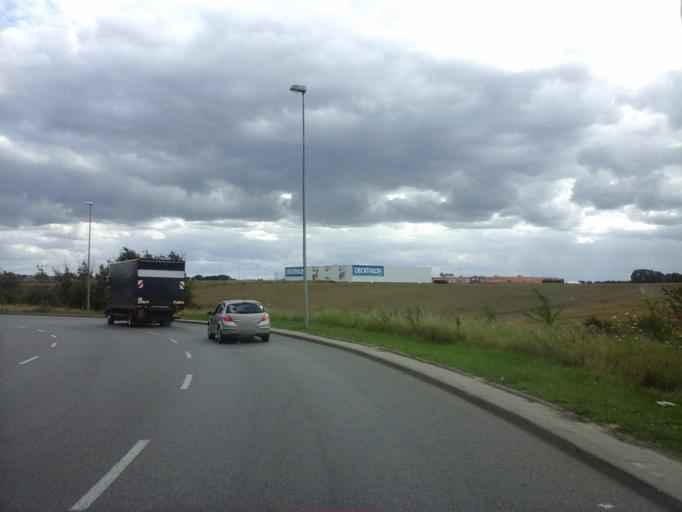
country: PL
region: West Pomeranian Voivodeship
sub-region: Powiat policki
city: Przeclaw
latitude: 53.3914
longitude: 14.5014
